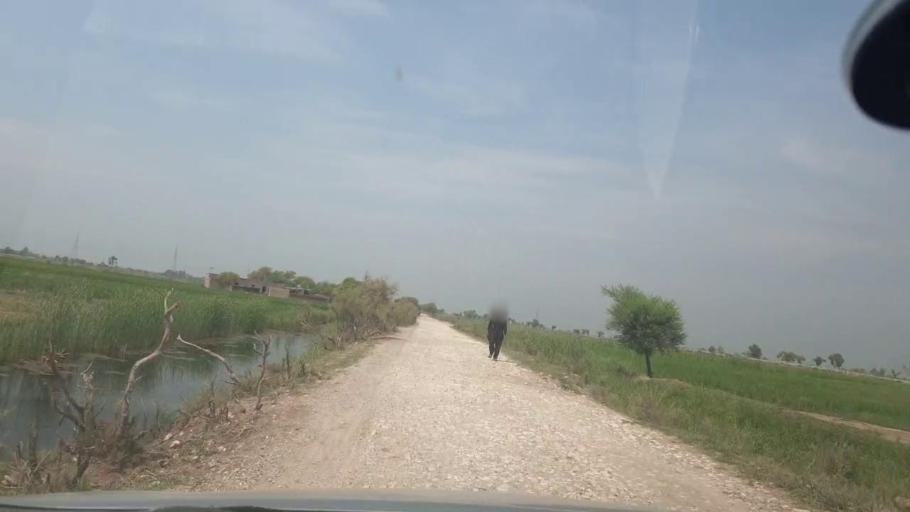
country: PK
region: Sindh
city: Thul
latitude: 28.1755
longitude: 68.6245
